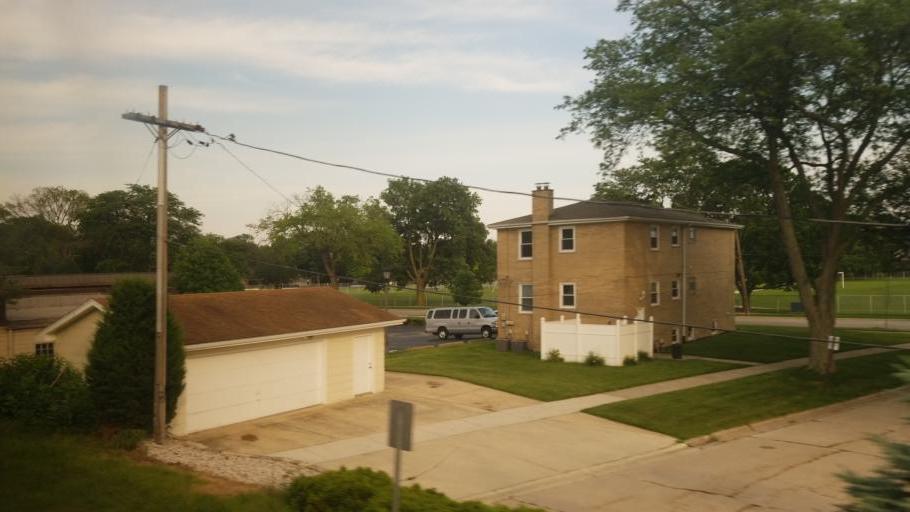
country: US
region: Illinois
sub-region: Cook County
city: Western Springs
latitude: 41.8121
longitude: -87.8879
